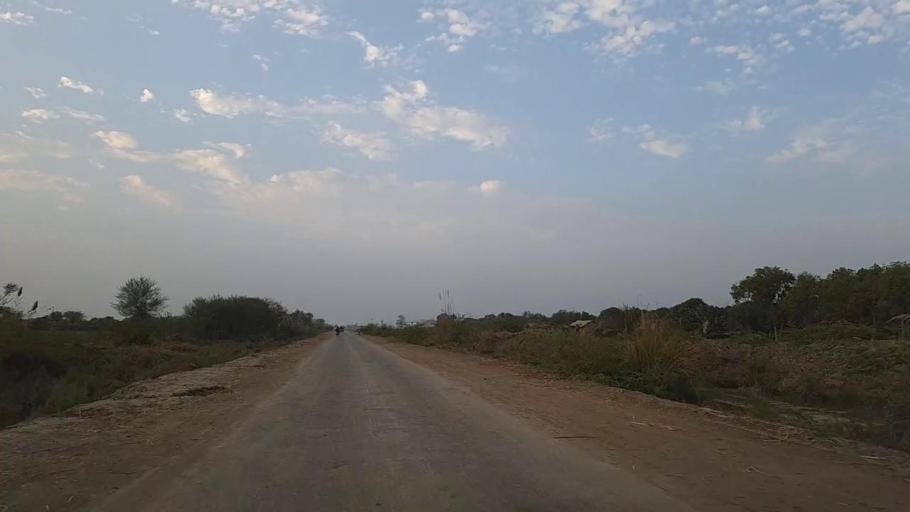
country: PK
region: Sindh
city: Mirwah Gorchani
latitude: 25.3237
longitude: 69.2178
